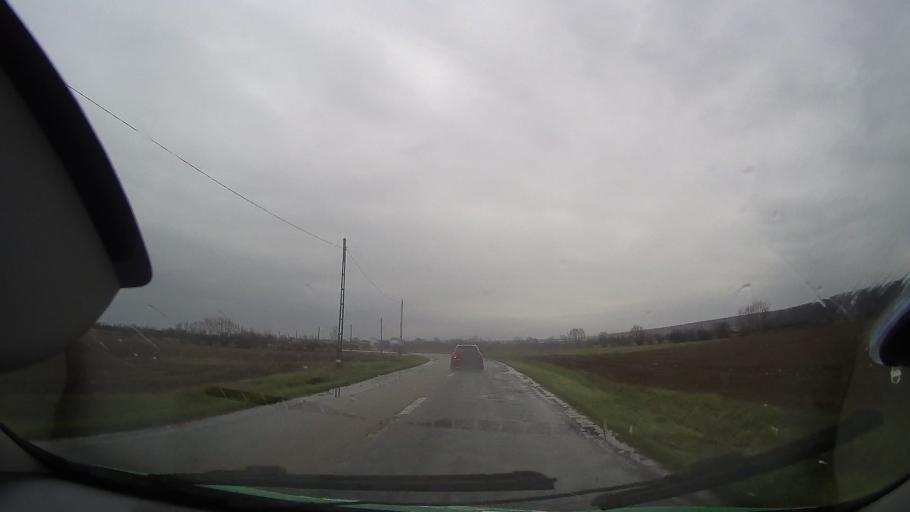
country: RO
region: Bihor
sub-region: Comuna Cociuba Mare
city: Cociuba Mare
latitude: 46.7413
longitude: 21.9816
